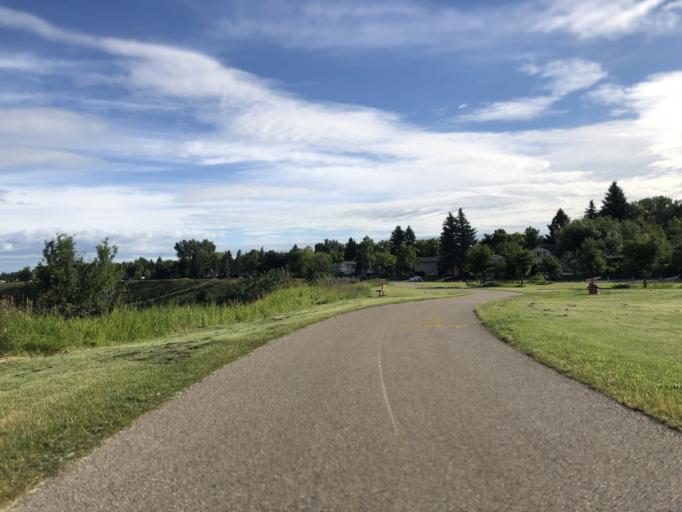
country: CA
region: Alberta
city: Calgary
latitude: 50.9879
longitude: -114.0204
